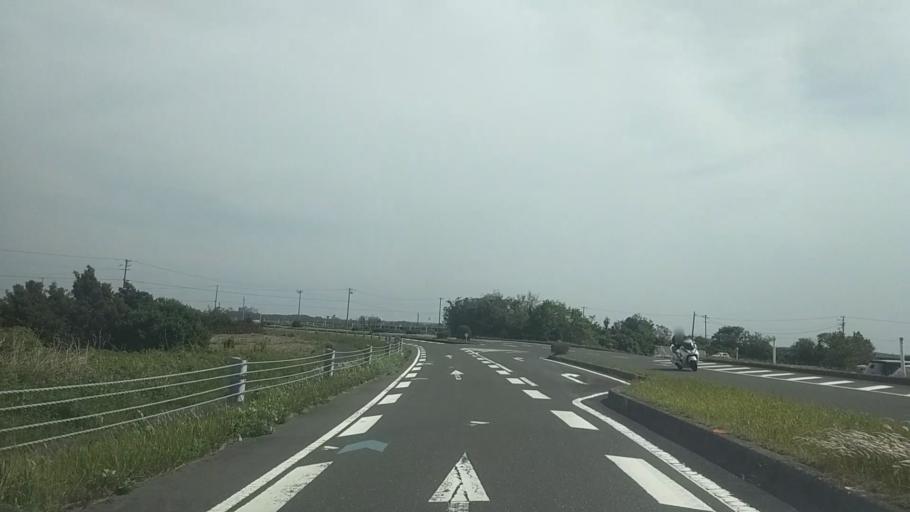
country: JP
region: Shizuoka
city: Kosai-shi
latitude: 34.7131
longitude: 137.5841
